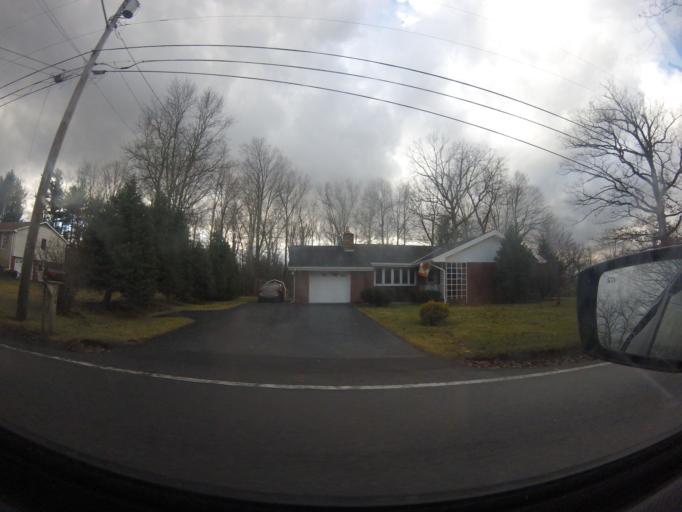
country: US
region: Maryland
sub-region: Garrett County
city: Mountain Lake Park
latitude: 39.4054
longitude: -79.3812
